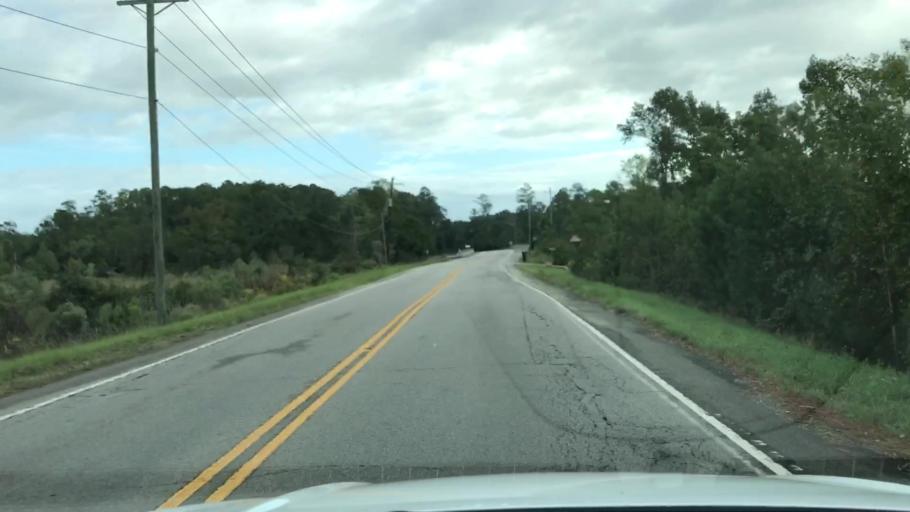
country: US
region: South Carolina
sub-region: Jasper County
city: Hardeeville
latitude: 32.2350
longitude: -81.0148
